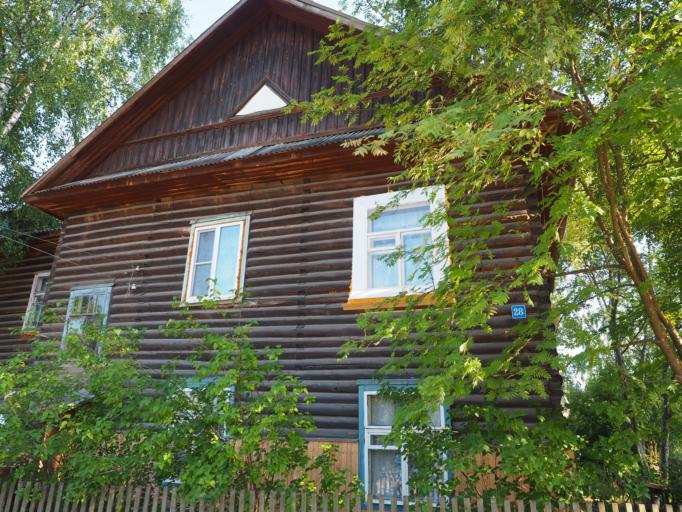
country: RU
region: Vologda
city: Chagoda
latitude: 59.1690
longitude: 35.3295
